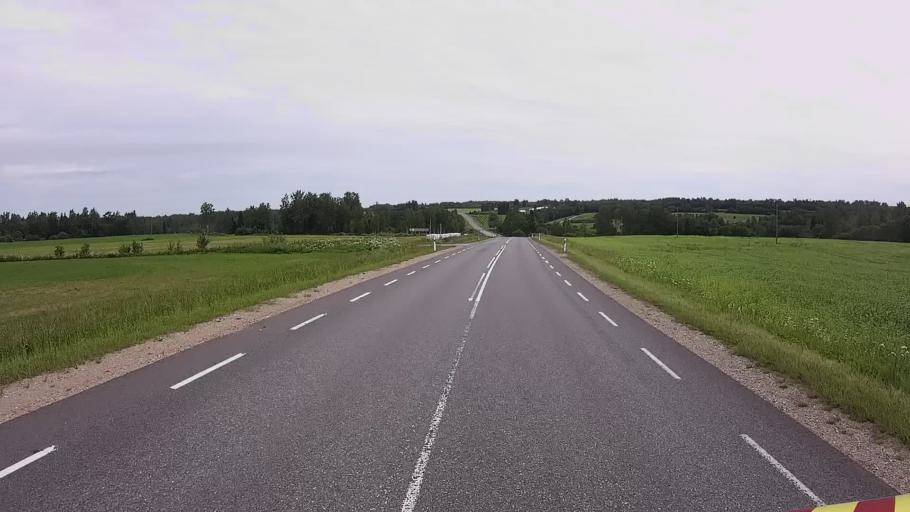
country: EE
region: Viljandimaa
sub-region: Karksi vald
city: Karksi-Nuia
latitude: 58.1431
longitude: 25.5881
